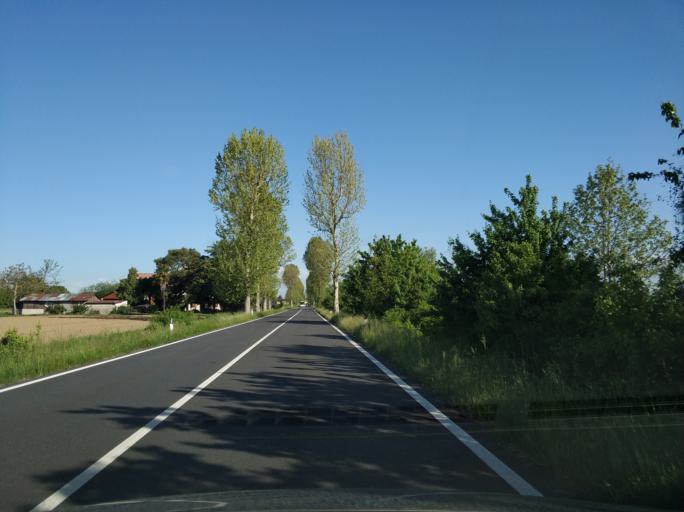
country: IT
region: Friuli Venezia Giulia
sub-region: Provincia di Udine
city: Terzo d'Aquileia
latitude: 45.7937
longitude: 13.3546
